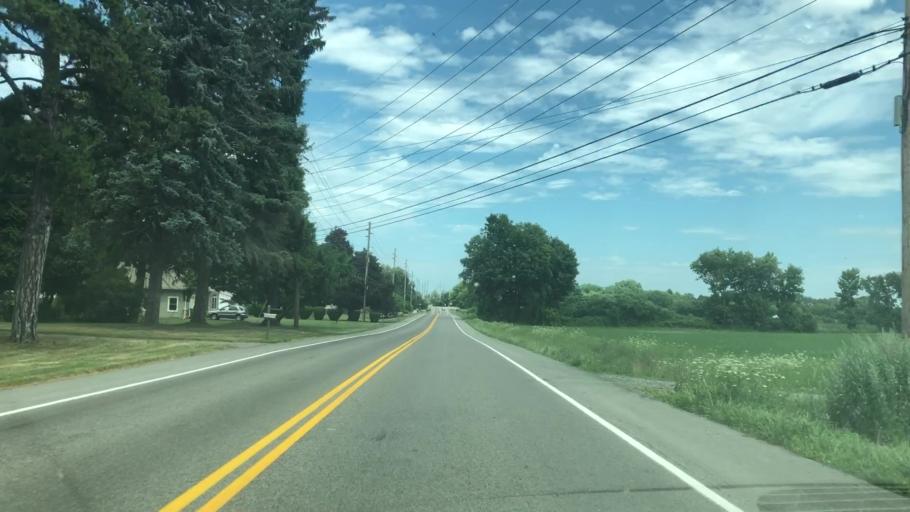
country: US
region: New York
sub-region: Monroe County
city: Webster
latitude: 43.2132
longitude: -77.4003
